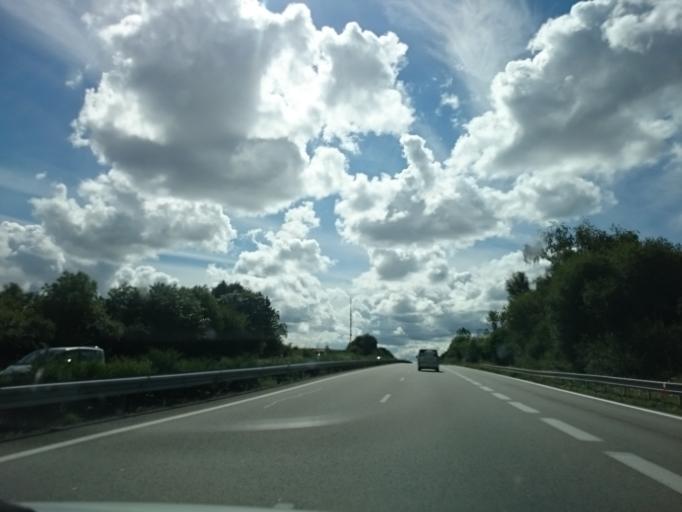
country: FR
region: Pays de la Loire
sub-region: Departement de la Loire-Atlantique
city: Mauves-sur-Loire
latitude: 47.3049
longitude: -1.4240
